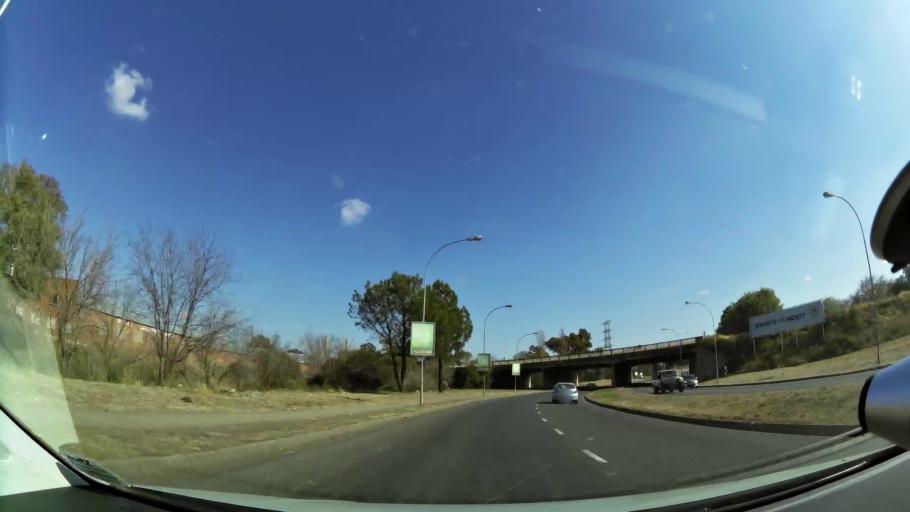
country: ZA
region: Orange Free State
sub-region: Mangaung Metropolitan Municipality
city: Bloemfontein
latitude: -29.1194
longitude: 26.2319
